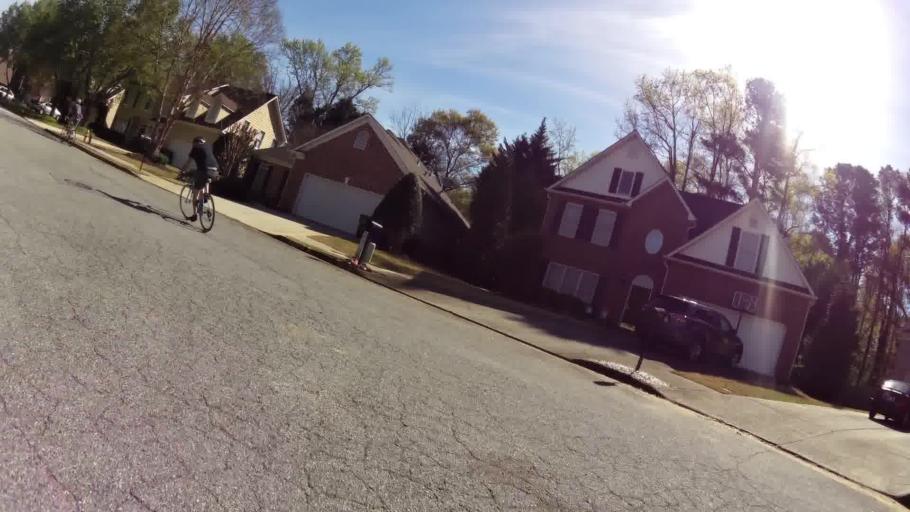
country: US
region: Georgia
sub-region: DeKalb County
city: Clarkston
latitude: 33.8220
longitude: -84.2666
